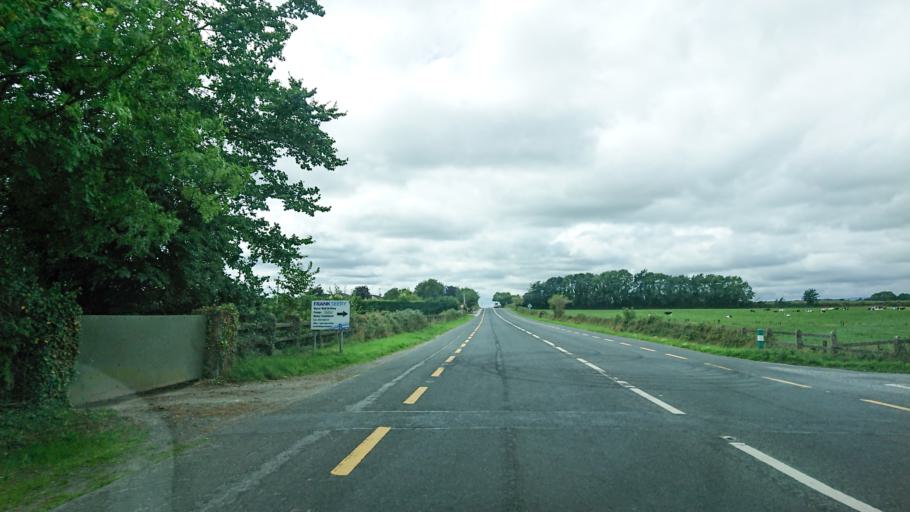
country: IE
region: Munster
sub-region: Waterford
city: Dungarvan
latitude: 52.1276
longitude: -7.7889
